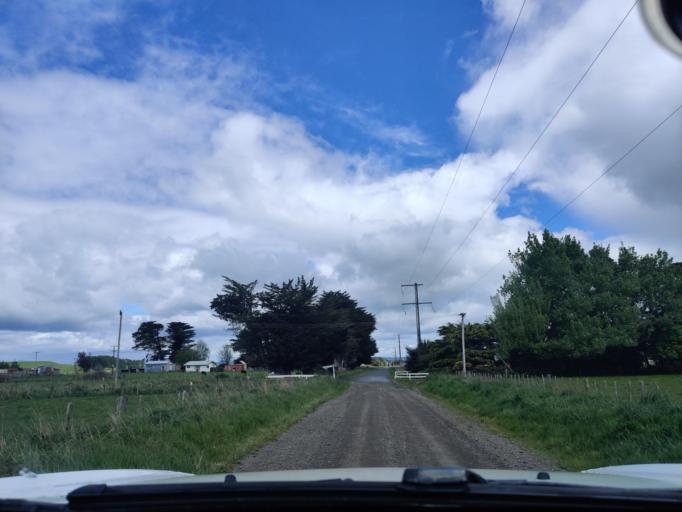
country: NZ
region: Manawatu-Wanganui
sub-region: Palmerston North City
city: Palmerston North
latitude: -40.3061
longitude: 175.8601
